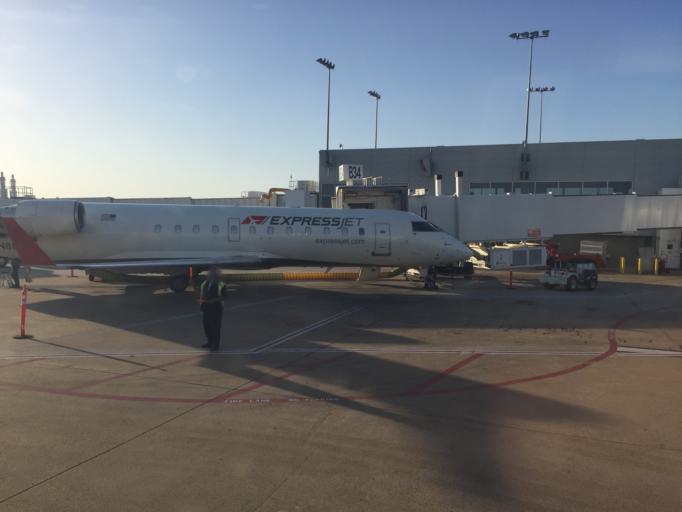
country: US
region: Texas
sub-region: Tarrant County
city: Grapevine
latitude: 32.9070
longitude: -97.0454
